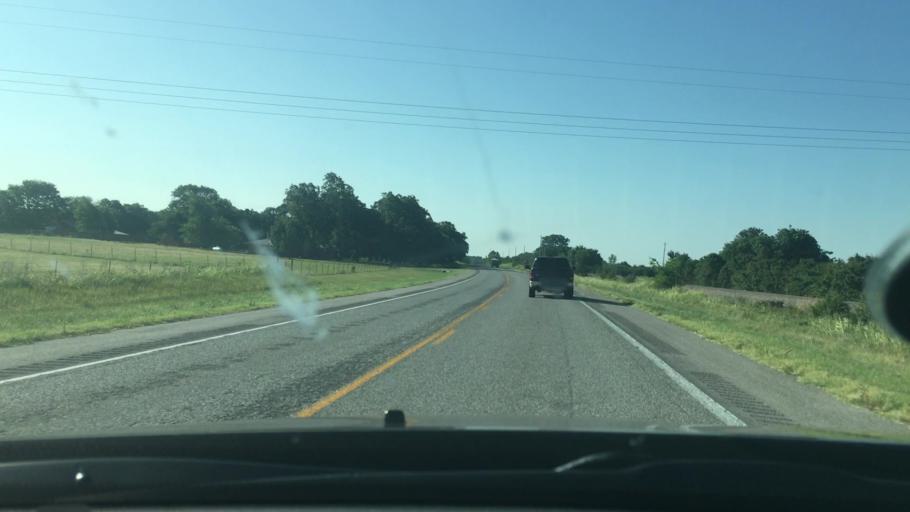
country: US
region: Oklahoma
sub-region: Johnston County
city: Tishomingo
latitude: 34.2618
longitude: -96.7702
